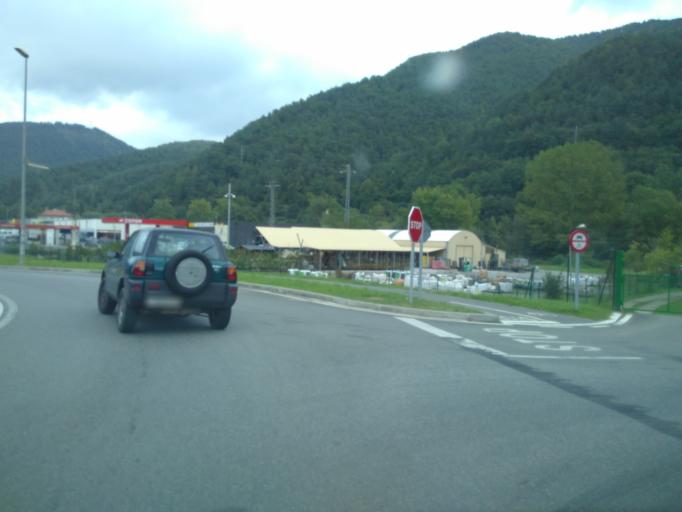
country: ES
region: Catalonia
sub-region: Provincia de Girona
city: Ripoll
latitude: 42.1837
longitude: 2.1958
